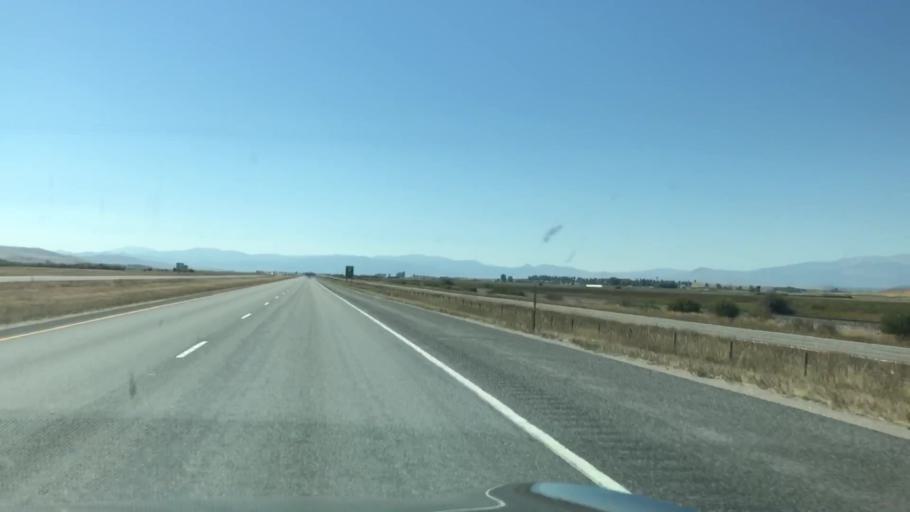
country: US
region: Montana
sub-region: Deer Lodge County
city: Warm Springs
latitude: 46.2572
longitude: -112.7586
